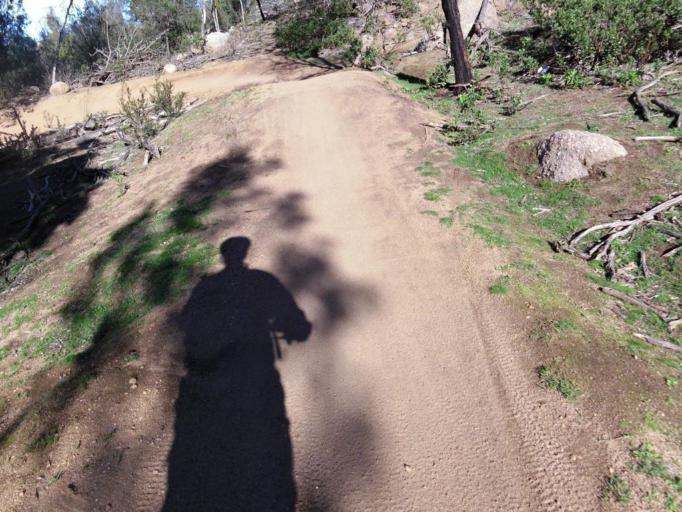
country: AU
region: Victoria
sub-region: Wyndham
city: Little River
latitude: -37.9358
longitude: 144.4389
